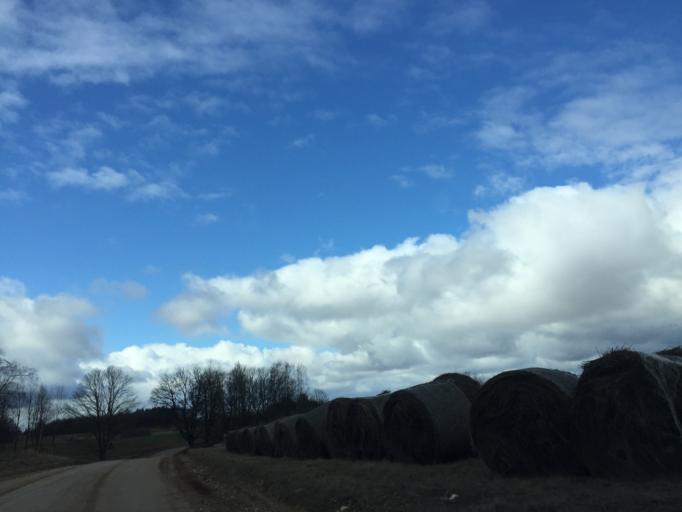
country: LV
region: Akniste
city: Akniste
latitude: 56.0916
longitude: 26.0001
